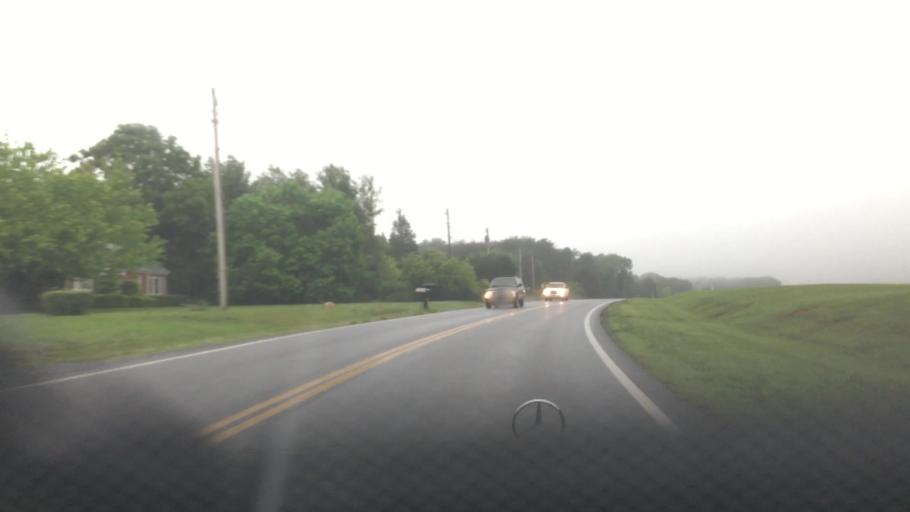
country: US
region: Virginia
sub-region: Campbell County
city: Timberlake
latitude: 37.3159
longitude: -79.2387
